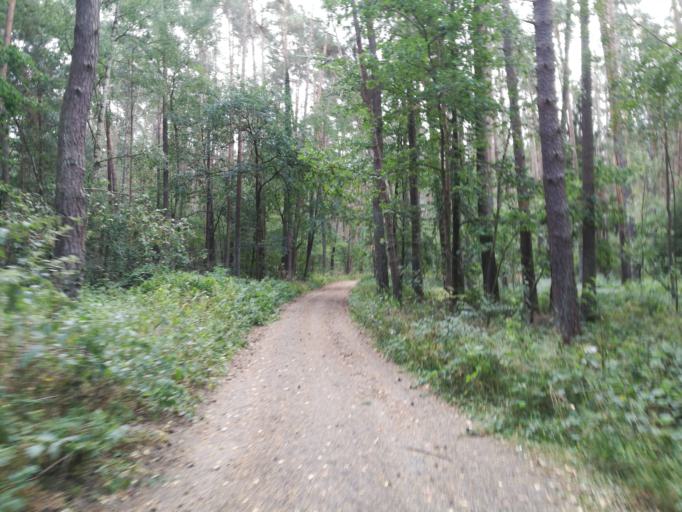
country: DE
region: Bavaria
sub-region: Regierungsbezirk Mittelfranken
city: Seukendorf
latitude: 49.4740
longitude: 10.8883
